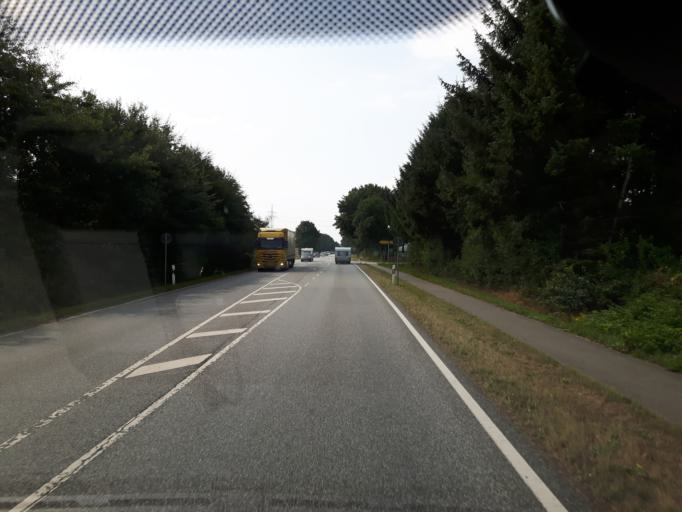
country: DE
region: Schleswig-Holstein
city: Goosefeld
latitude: 54.4294
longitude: 9.8086
